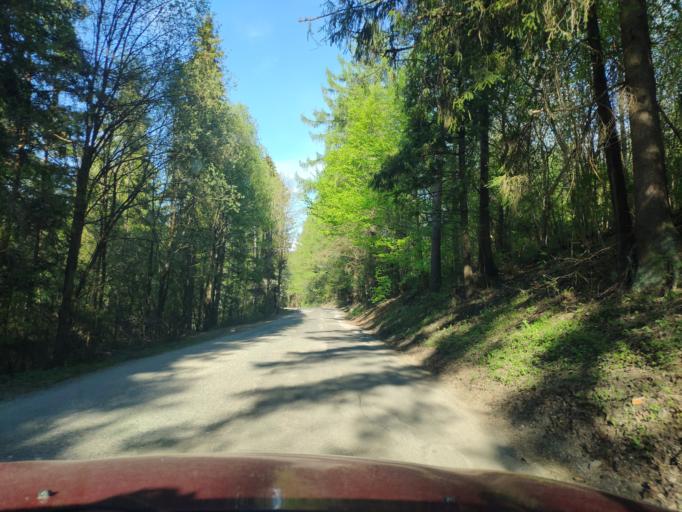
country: SK
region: Presovsky
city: Spisske Podhradie
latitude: 49.0330
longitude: 20.8031
